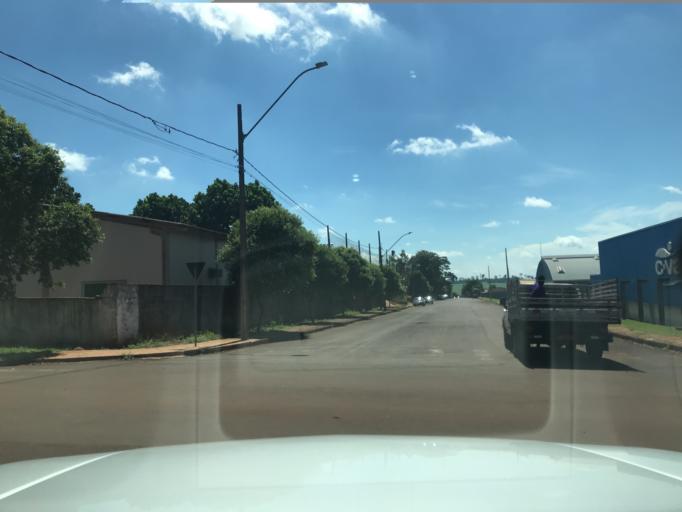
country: BR
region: Parana
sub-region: Palotina
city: Palotina
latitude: -24.2838
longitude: -53.8337
